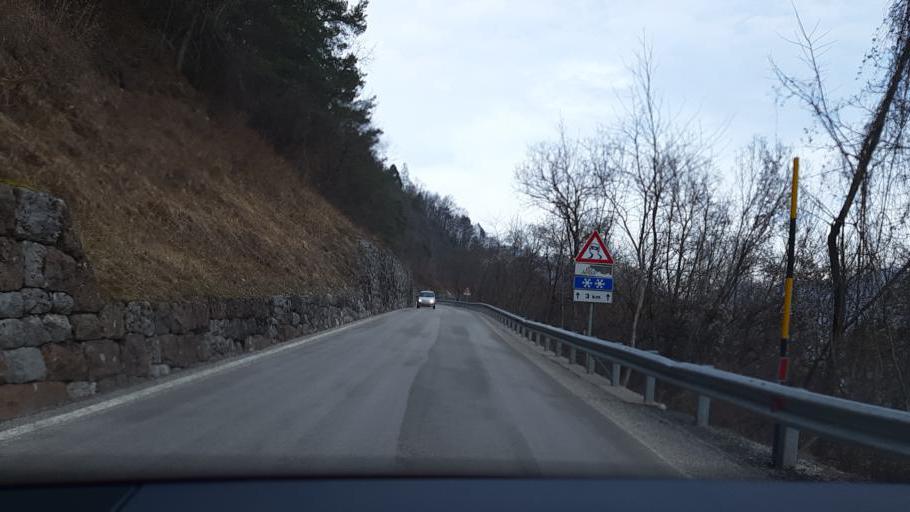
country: IT
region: Trentino-Alto Adige
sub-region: Provincia di Trento
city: Borgo
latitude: 46.0335
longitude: 11.4554
